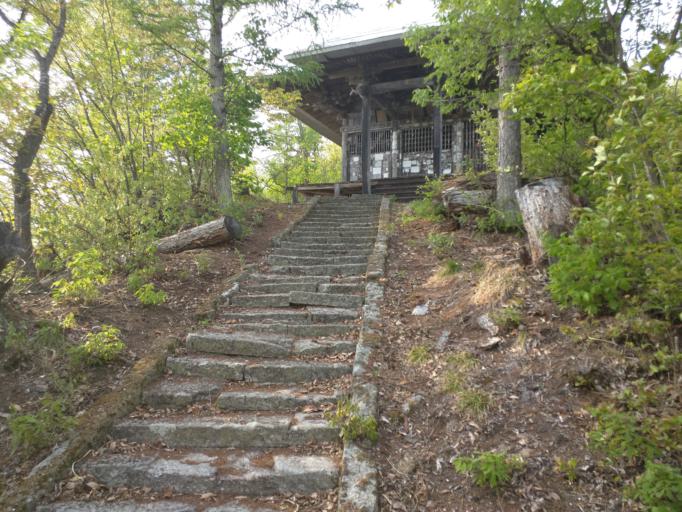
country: JP
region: Fukushima
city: Kitakata
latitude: 37.4457
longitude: 139.8800
